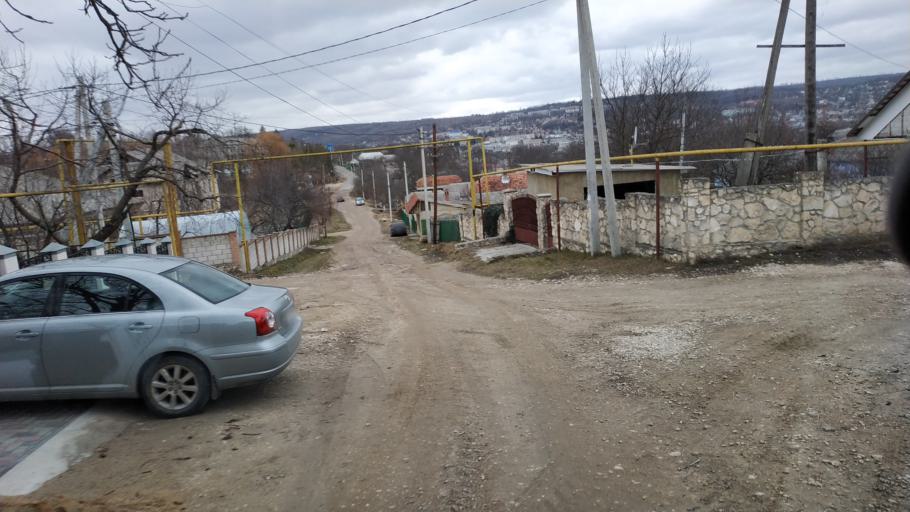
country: MD
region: Calarasi
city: Calarasi
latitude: 47.2365
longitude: 28.3103
